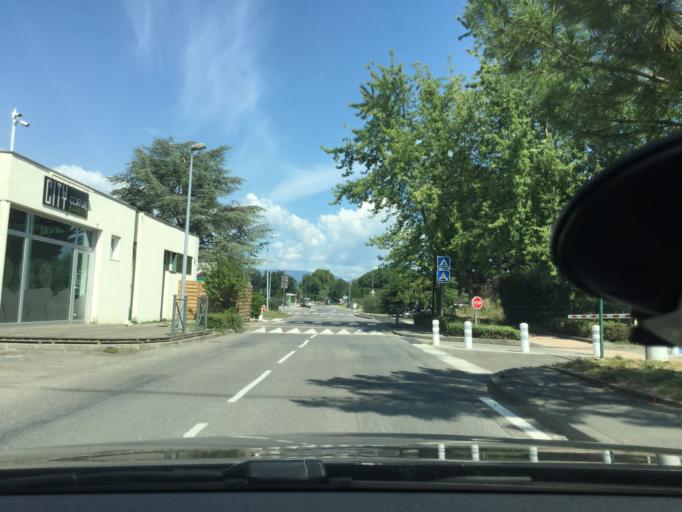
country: FR
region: Rhone-Alpes
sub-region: Departement de la Haute-Savoie
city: Veigy-Foncenex
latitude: 46.2755
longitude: 6.2481
